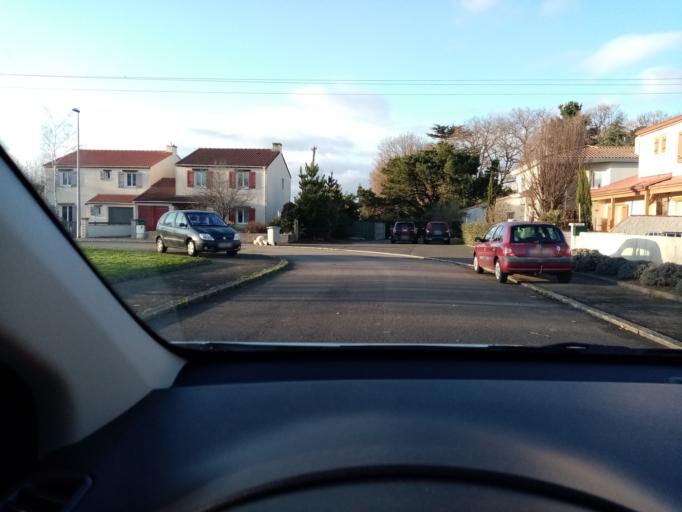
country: FR
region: Pays de la Loire
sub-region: Departement de la Loire-Atlantique
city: Saint-Sebastien-sur-Loire
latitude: 47.1935
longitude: -1.5042
